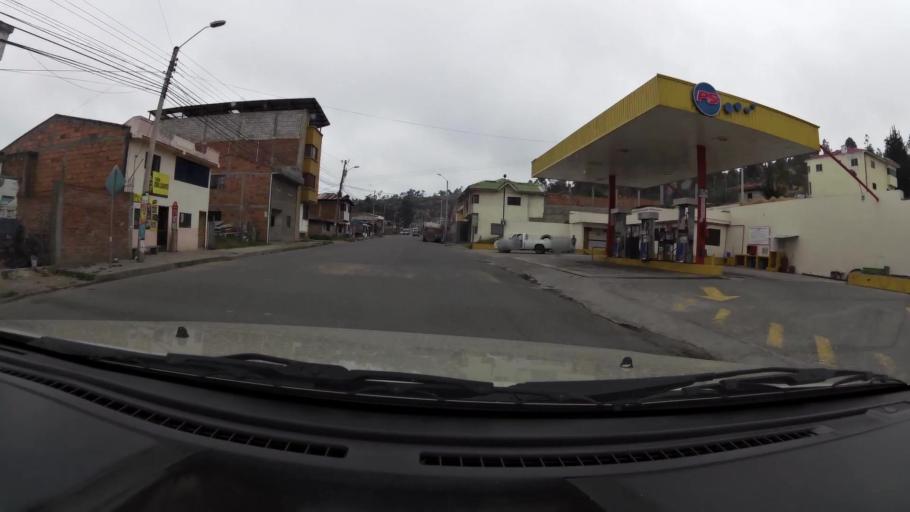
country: EC
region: Canar
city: Canar
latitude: -2.5034
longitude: -78.9271
